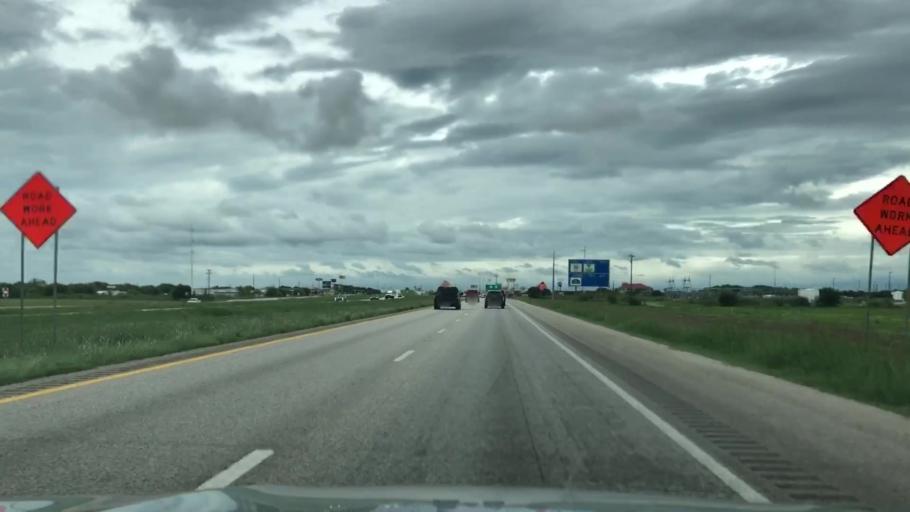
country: US
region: Texas
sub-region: Guadalupe County
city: McQueeney
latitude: 29.5776
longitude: -98.0034
